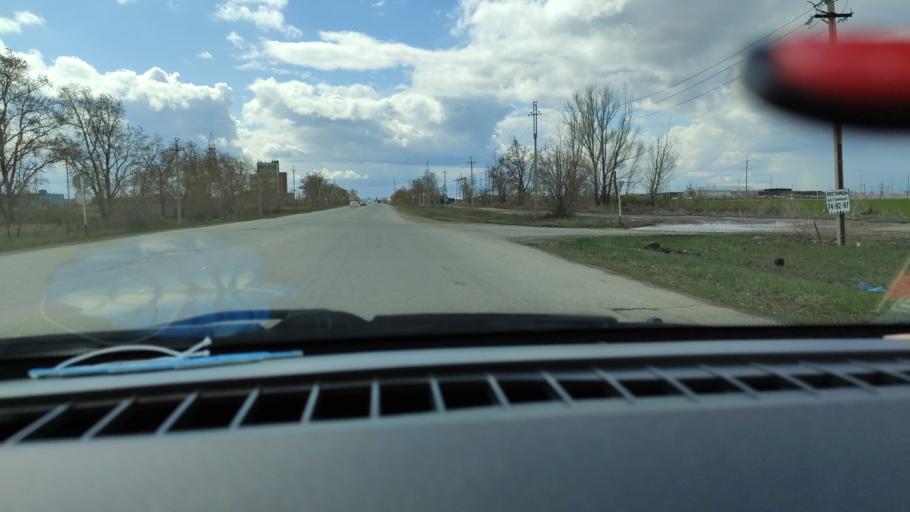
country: RU
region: Samara
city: Tol'yatti
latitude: 53.5843
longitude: 49.4045
